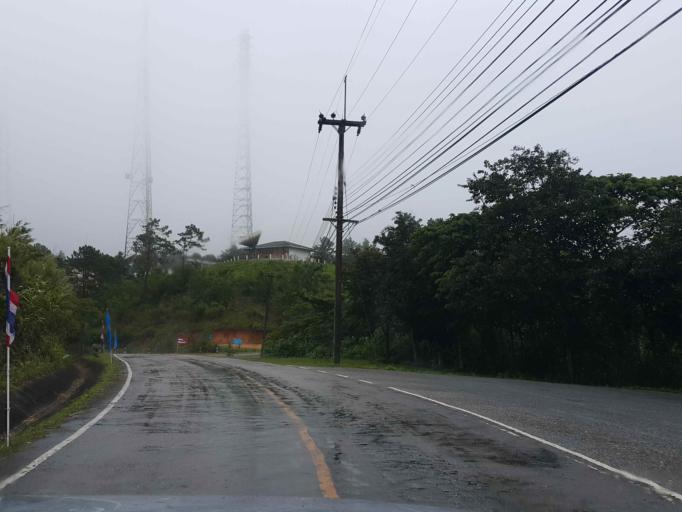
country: TH
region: Tak
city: Tak
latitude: 16.7767
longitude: 98.9285
